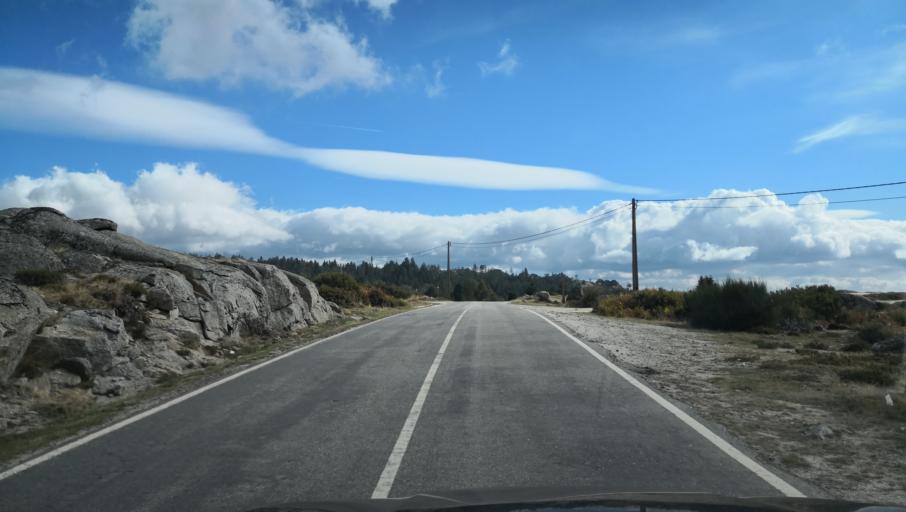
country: PT
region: Vila Real
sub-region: Vila Real
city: Vila Real
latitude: 41.3577
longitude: -7.7957
